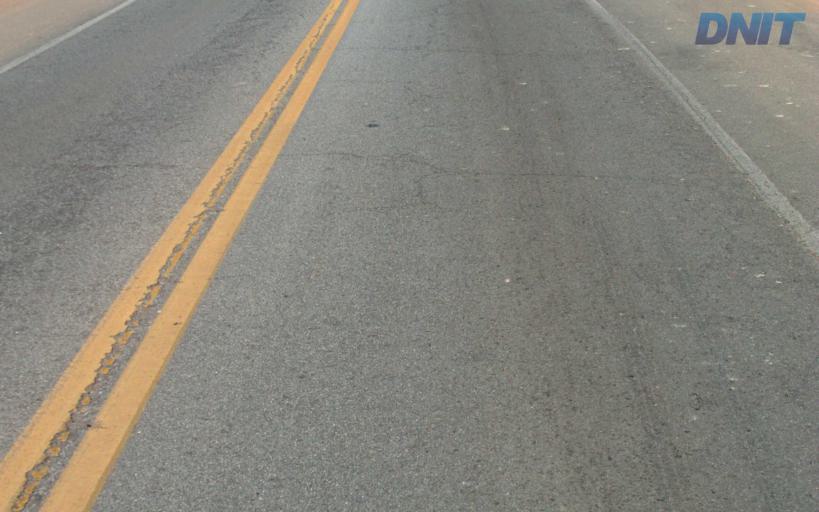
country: BR
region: Minas Gerais
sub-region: Barao De Cocais
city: Barao de Cocais
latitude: -19.7487
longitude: -43.4906
